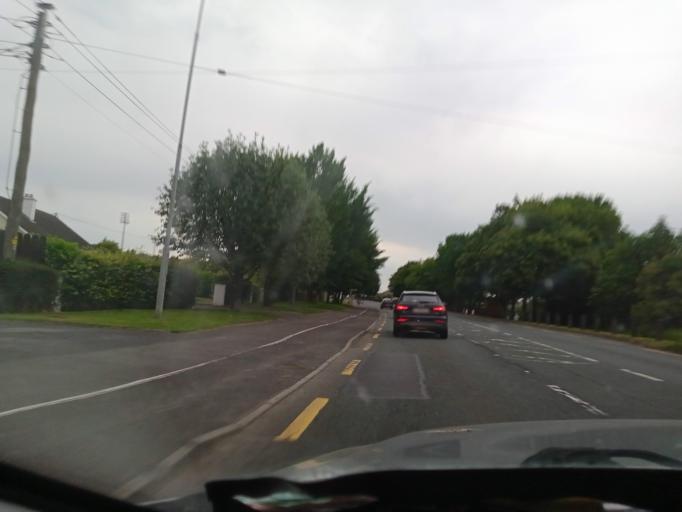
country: IE
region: Leinster
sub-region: Laois
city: Portlaoise
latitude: 53.0227
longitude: -7.2993
